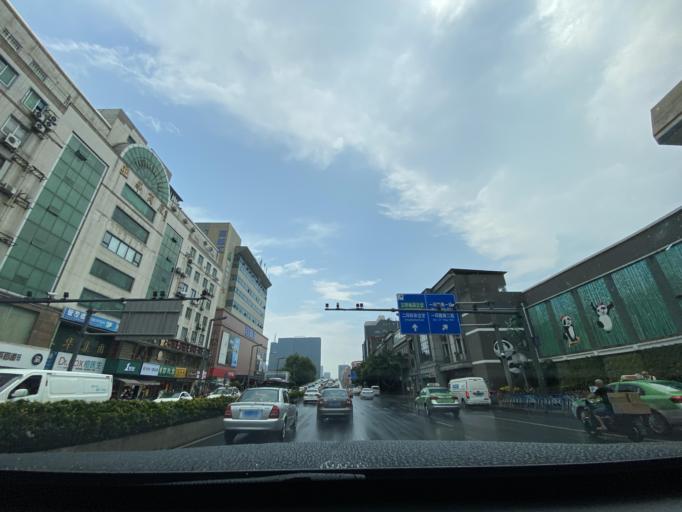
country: CN
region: Sichuan
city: Chengdu
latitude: 30.6386
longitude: 104.0735
